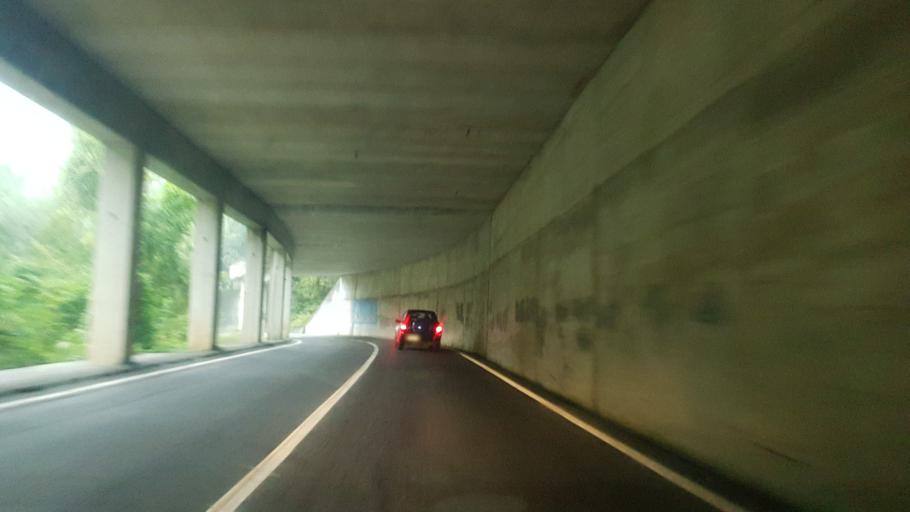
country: IT
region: Piedmont
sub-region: Provincia di Cuneo
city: Frabosa Soprana
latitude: 44.2678
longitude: 7.7688
